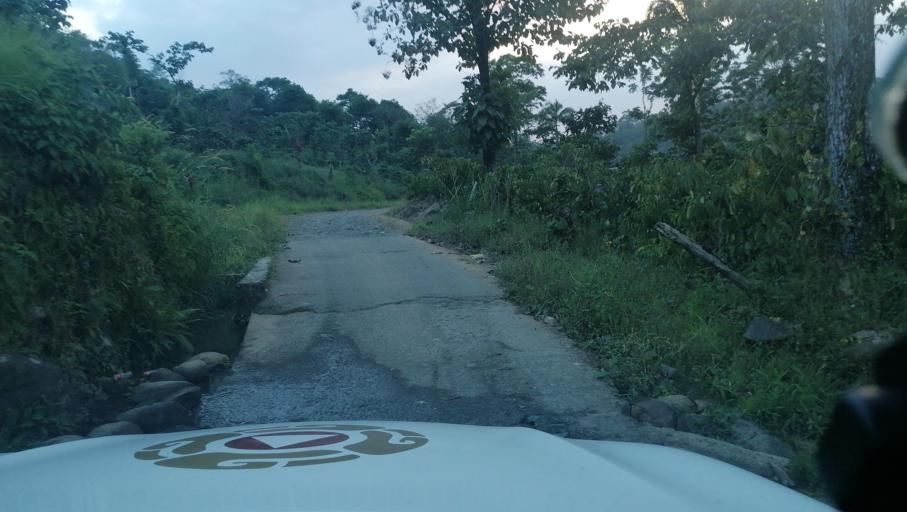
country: MX
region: Chiapas
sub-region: Cacahoatan
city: Benito Juarez
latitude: 15.0653
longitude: -92.2352
